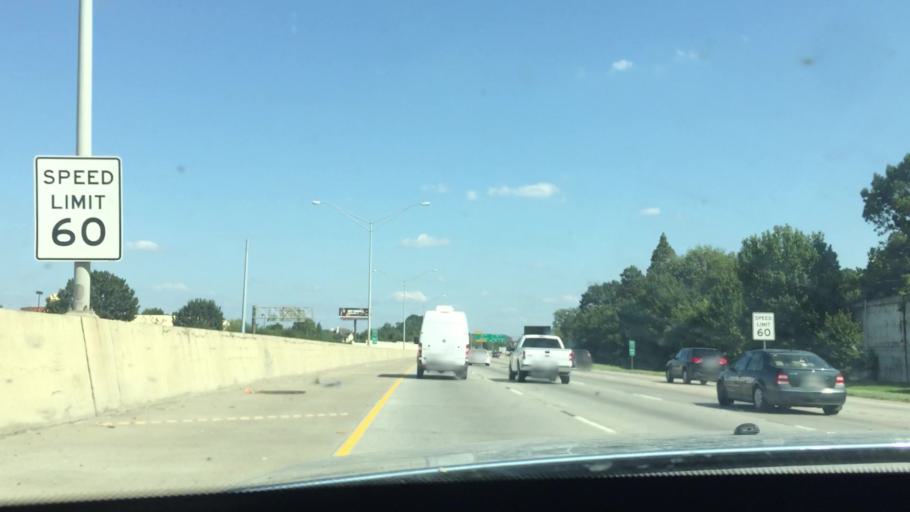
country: US
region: Louisiana
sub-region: East Baton Rouge Parish
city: Baton Rouge
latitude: 30.4219
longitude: -91.1295
